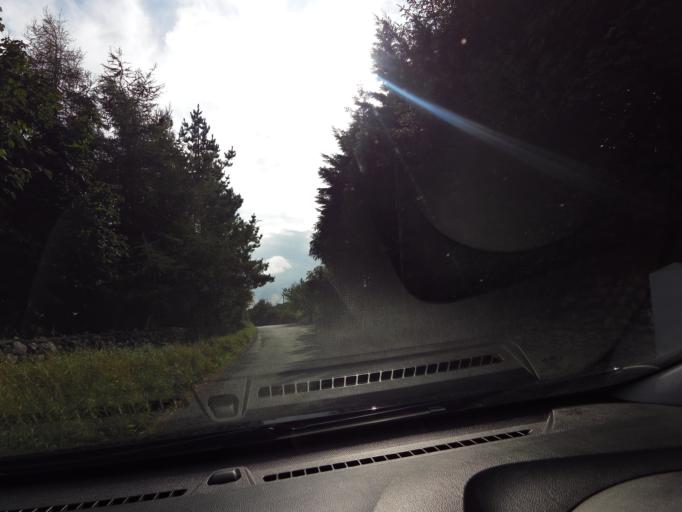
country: IE
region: Connaught
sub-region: County Galway
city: Oranmore
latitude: 53.2874
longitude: -8.8526
